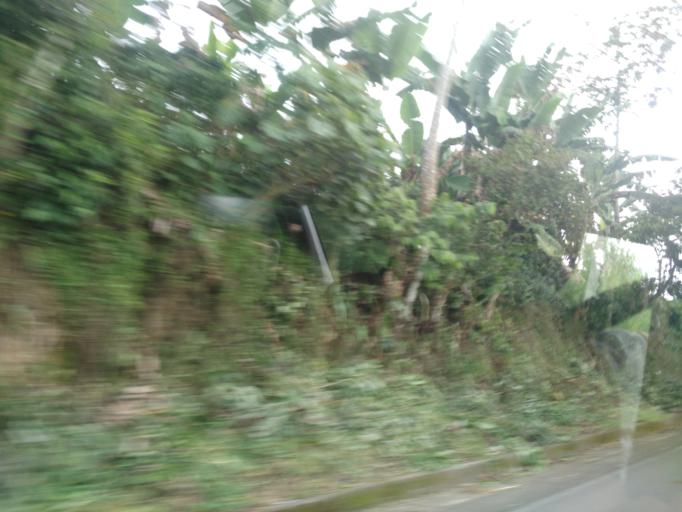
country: CO
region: Valle del Cauca
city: Sevilla
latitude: 4.2687
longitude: -75.9199
